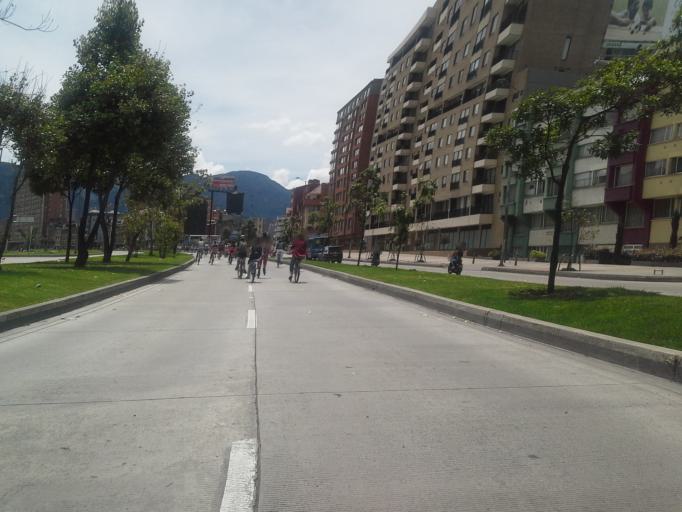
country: CO
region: Bogota D.C.
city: Bogota
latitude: 4.6365
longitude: -74.0927
